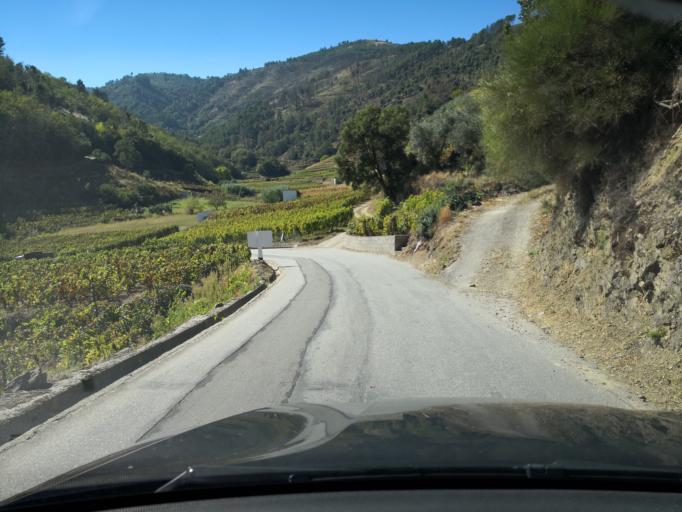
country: PT
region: Vila Real
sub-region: Santa Marta de Penaguiao
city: Santa Marta de Penaguiao
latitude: 41.2440
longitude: -7.8167
